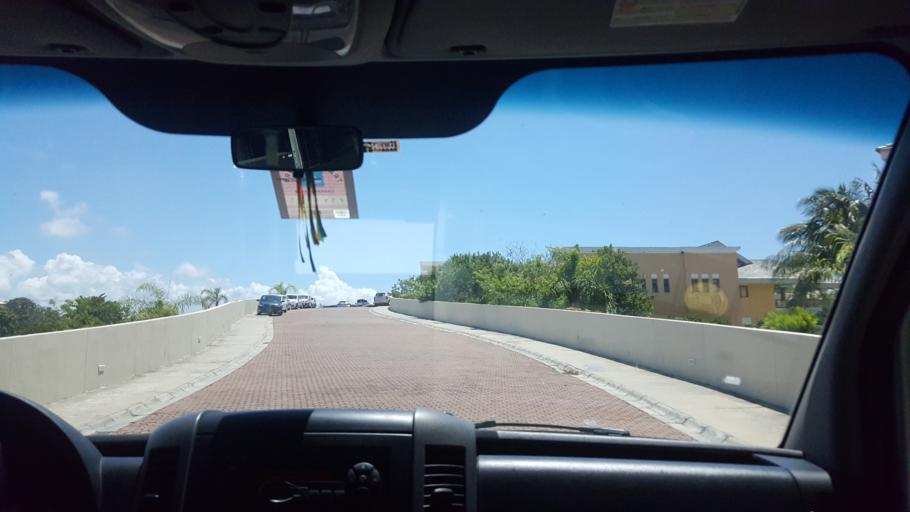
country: BR
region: Bahia
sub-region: Mata De Sao Joao
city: Mata de Sao Joao
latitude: -12.5470
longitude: -37.9874
